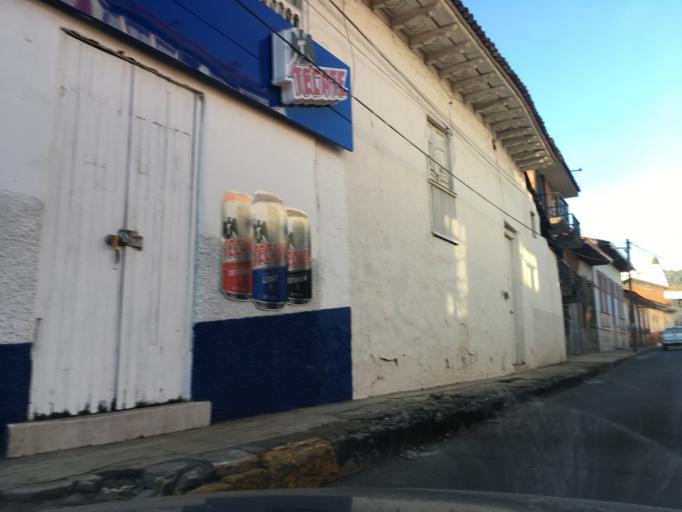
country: MX
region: Michoacan
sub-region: Uruapan
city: Uruapan
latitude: 19.4207
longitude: -102.0663
